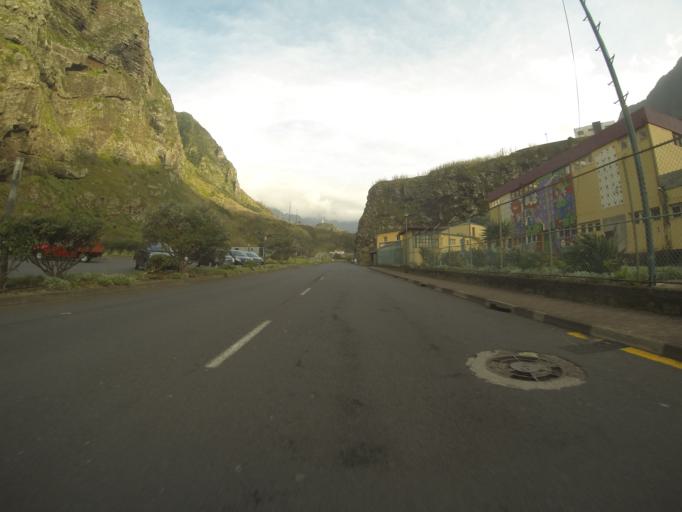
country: PT
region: Madeira
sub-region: Sao Vicente
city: Sao Vicente
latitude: 32.8069
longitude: -17.0471
